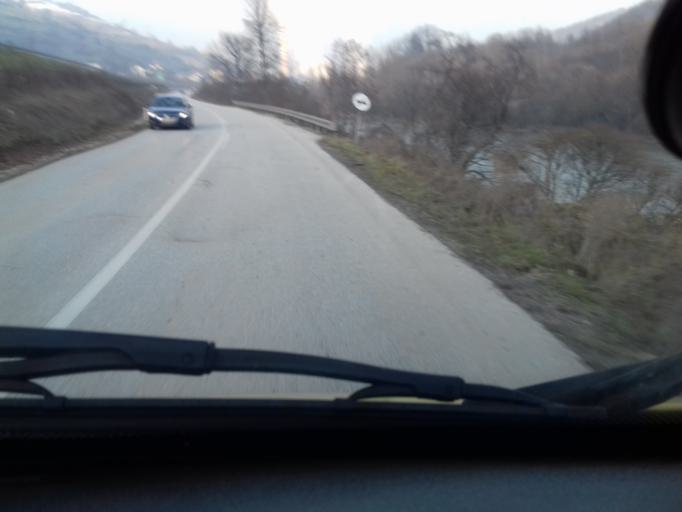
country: BA
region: Federation of Bosnia and Herzegovina
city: Dobrinje
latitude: 44.0732
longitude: 18.1081
